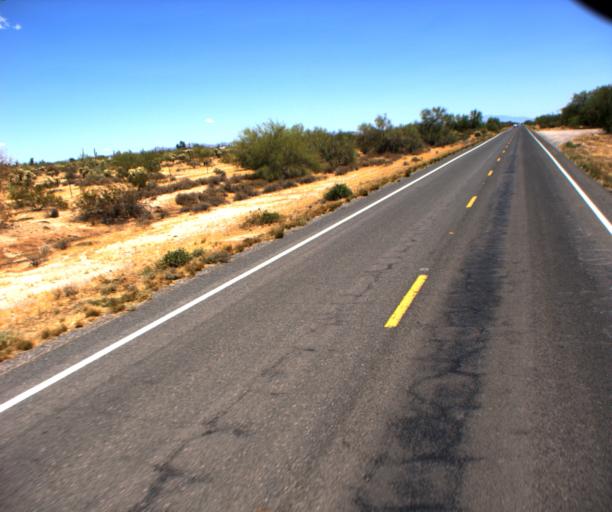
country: US
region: Arizona
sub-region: Pinal County
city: Florence
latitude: 32.9503
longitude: -111.3258
